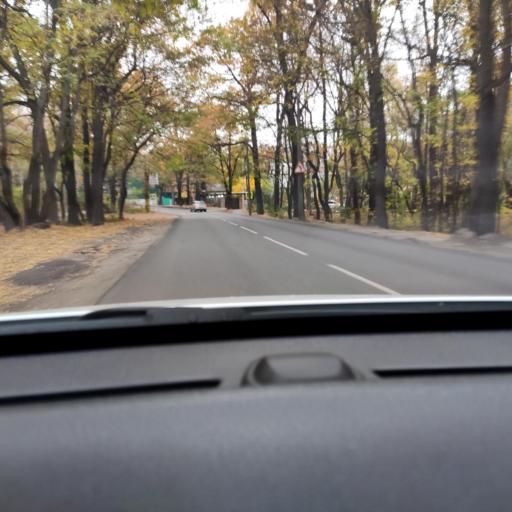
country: RU
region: Voronezj
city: Voronezh
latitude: 51.7222
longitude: 39.2222
